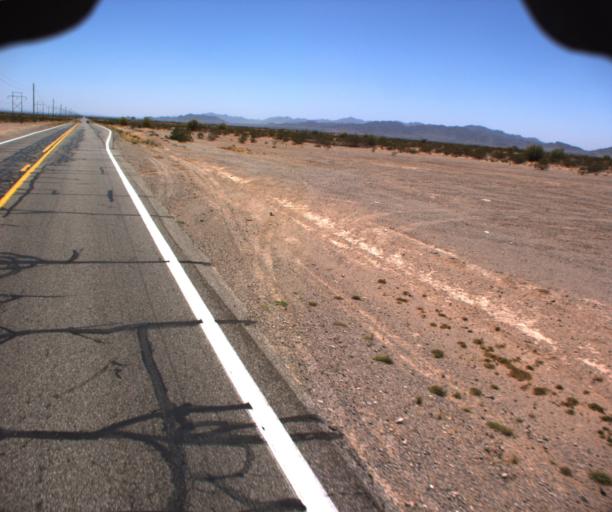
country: US
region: Arizona
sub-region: La Paz County
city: Quartzsite
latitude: 33.8192
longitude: -114.2170
